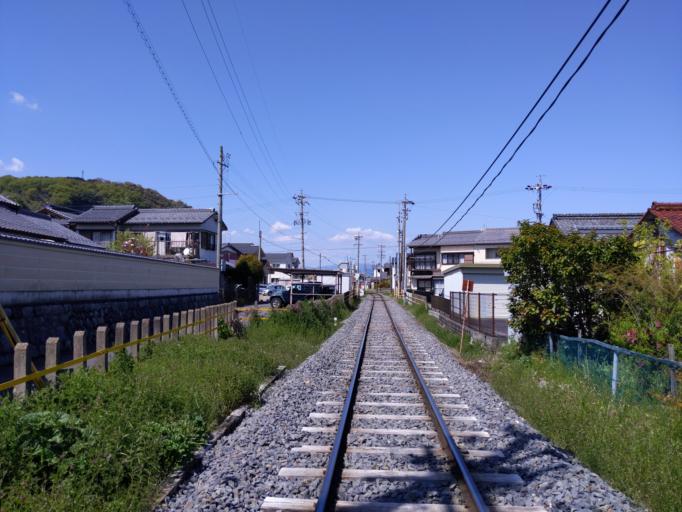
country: JP
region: Gifu
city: Godo
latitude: 35.3912
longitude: 136.5830
